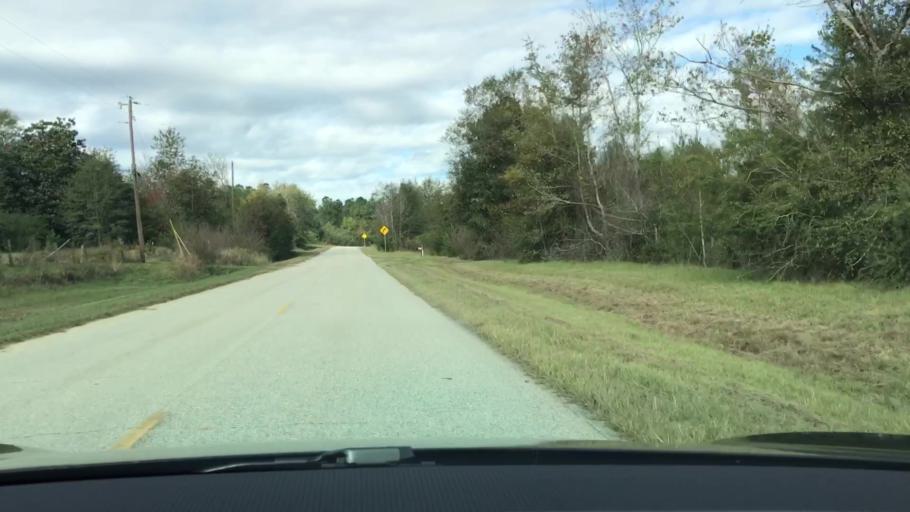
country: US
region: Georgia
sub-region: Jefferson County
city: Wadley
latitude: 32.8006
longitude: -82.3828
